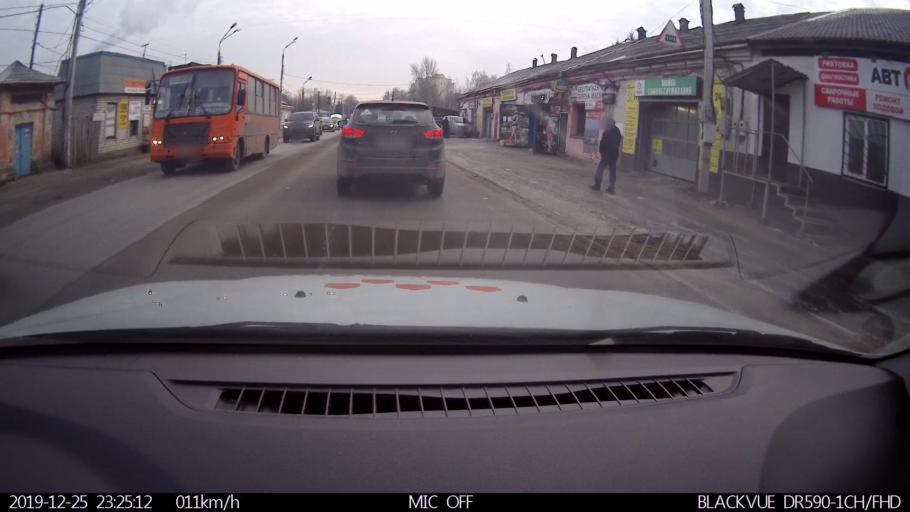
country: RU
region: Nizjnij Novgorod
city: Gorbatovka
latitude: 56.3489
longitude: 43.8366
